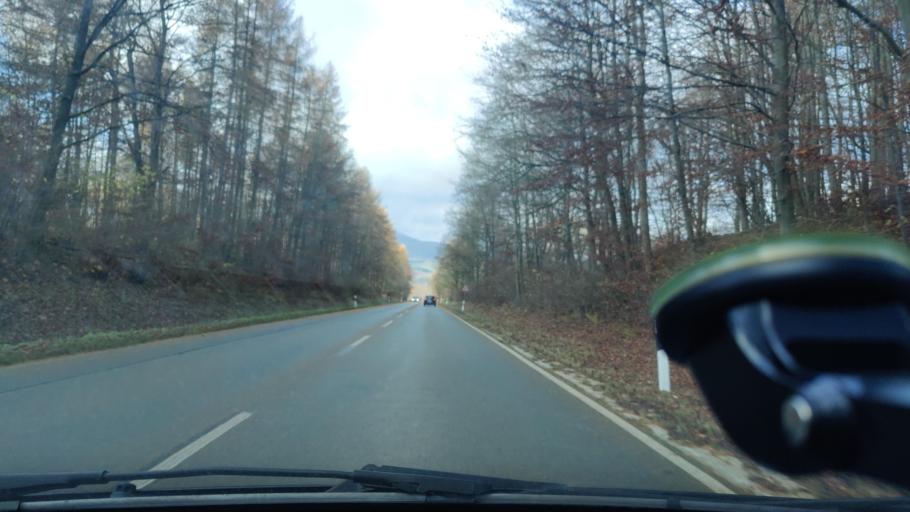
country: DE
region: Hesse
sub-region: Regierungsbezirk Kassel
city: Zierenberg
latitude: 51.3239
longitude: 9.3348
